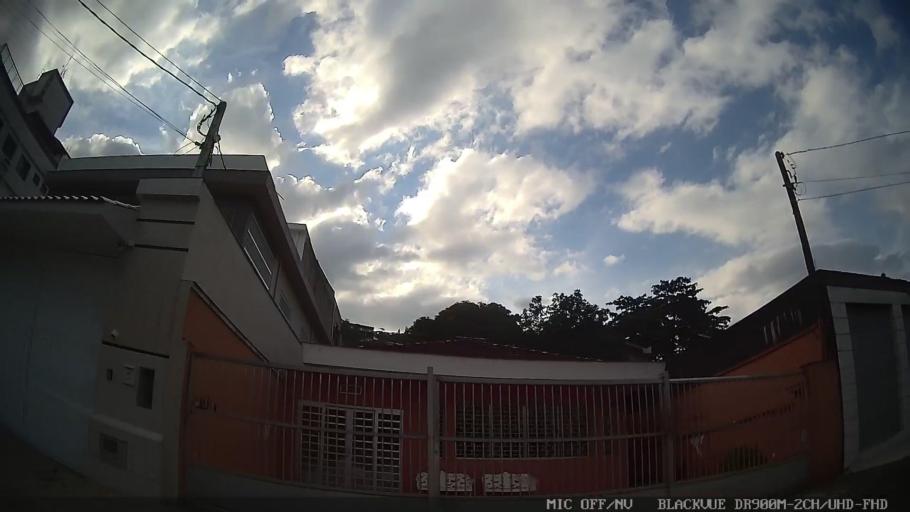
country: BR
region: Sao Paulo
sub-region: Guaruja
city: Guaruja
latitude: -23.9818
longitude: -46.2388
